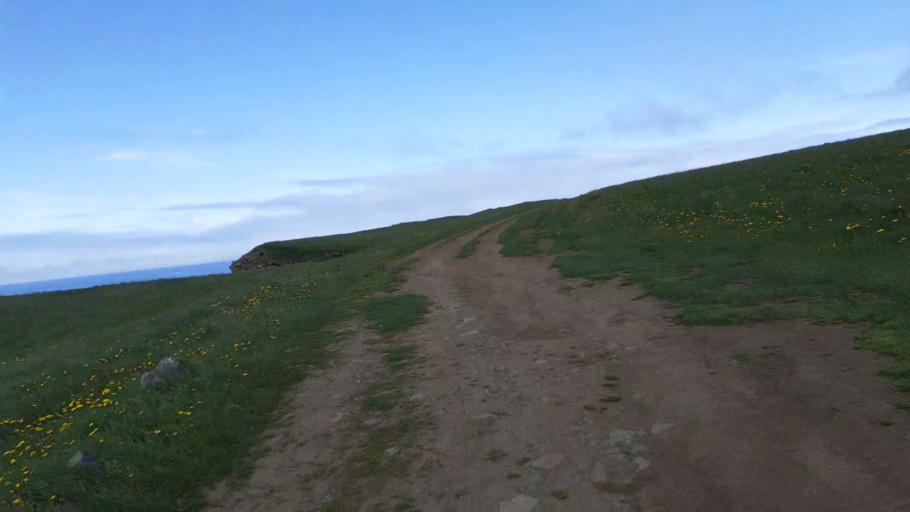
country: IS
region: Northeast
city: Dalvik
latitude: 66.5540
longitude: -18.0125
